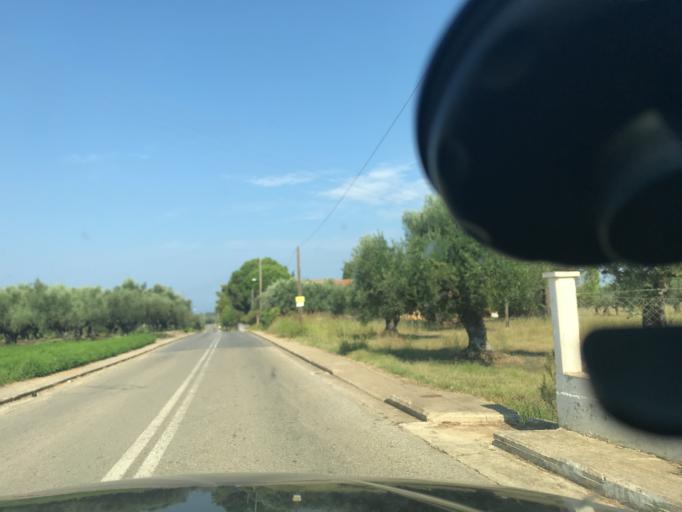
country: GR
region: West Greece
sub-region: Nomos Ileias
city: Kardamas
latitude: 37.7177
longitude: 21.3305
